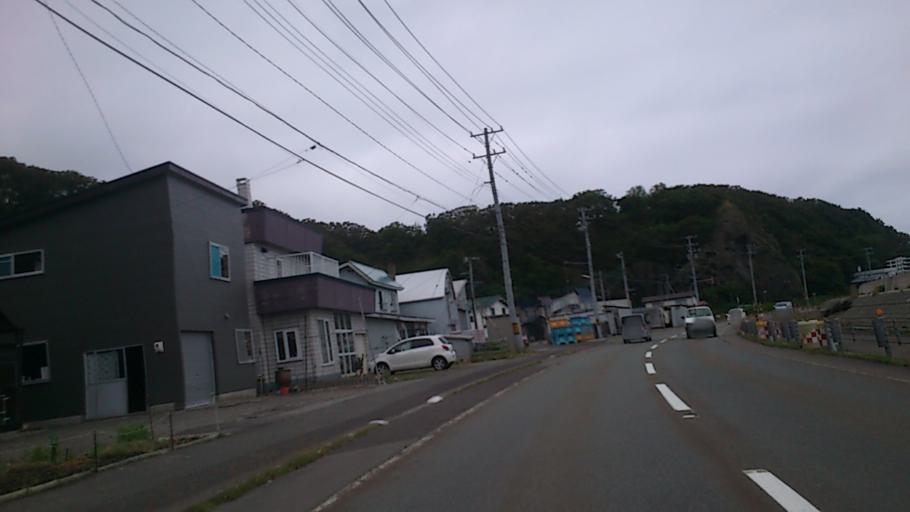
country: JP
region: Hokkaido
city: Iwanai
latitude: 42.7351
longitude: 140.1008
